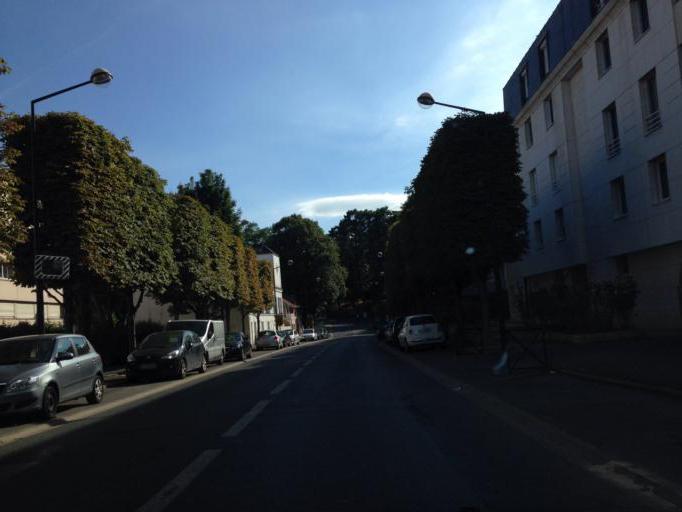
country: FR
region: Ile-de-France
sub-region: Departement des Hauts-de-Seine
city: Meudon
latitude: 48.8048
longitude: 2.2353
